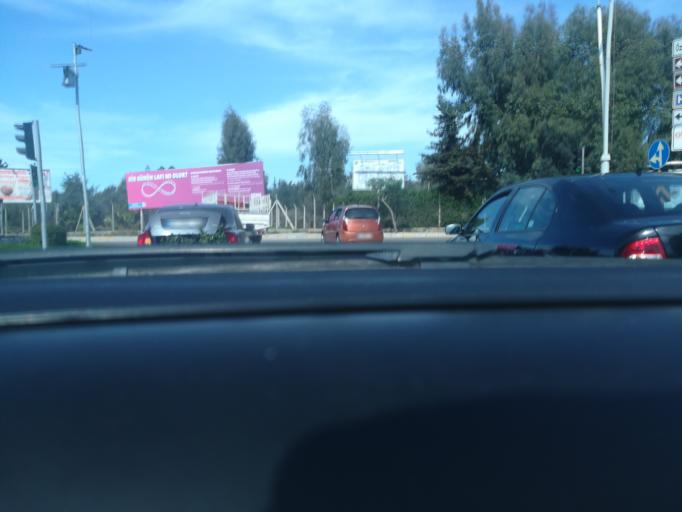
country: TR
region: Adana
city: Adana
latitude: 37.0303
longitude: 35.3232
